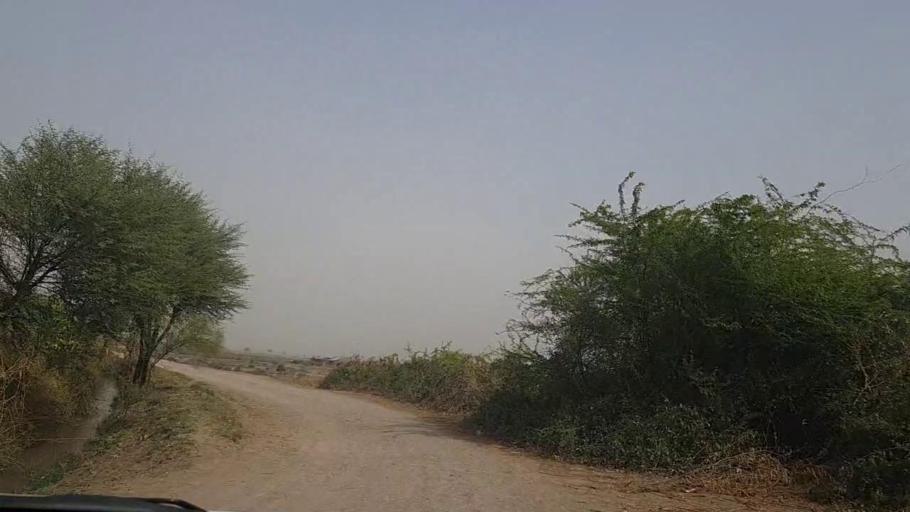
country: PK
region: Sindh
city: Pithoro
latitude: 25.4514
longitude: 69.2370
